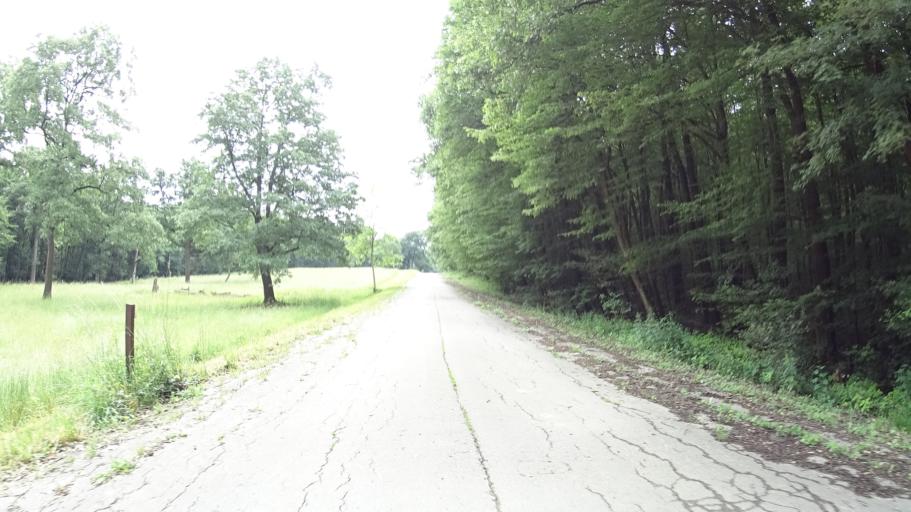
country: HU
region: Pest
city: Nagymaros
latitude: 47.8047
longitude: 18.9419
